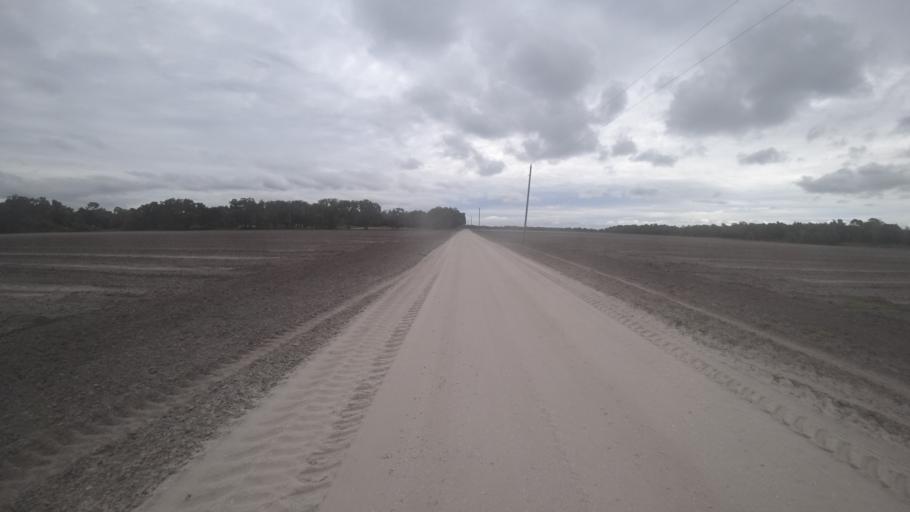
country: US
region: Florida
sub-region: Hillsborough County
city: Wimauma
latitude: 27.5798
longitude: -82.1278
